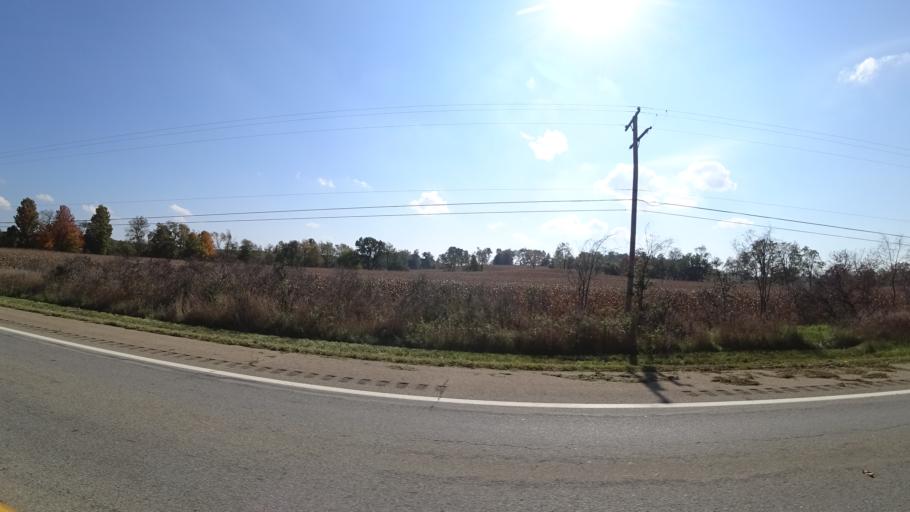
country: US
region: Michigan
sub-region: Jackson County
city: Concord
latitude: 42.1625
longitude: -84.7229
